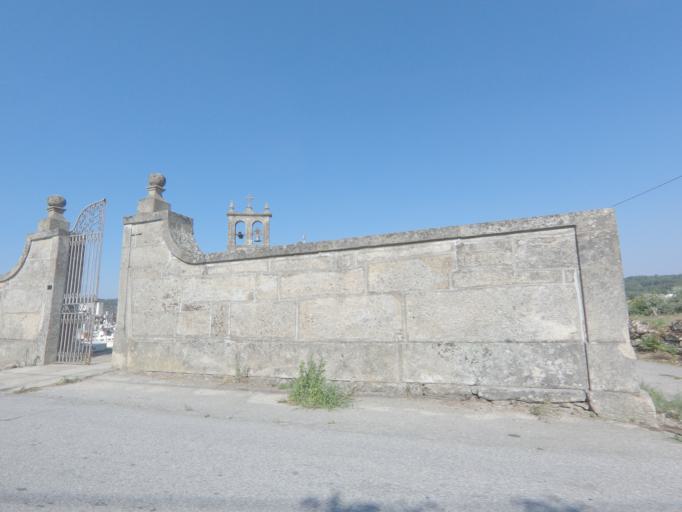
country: PT
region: Viseu
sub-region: Moimenta da Beira
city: Moimenta da Beira
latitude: 40.9731
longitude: -7.5914
